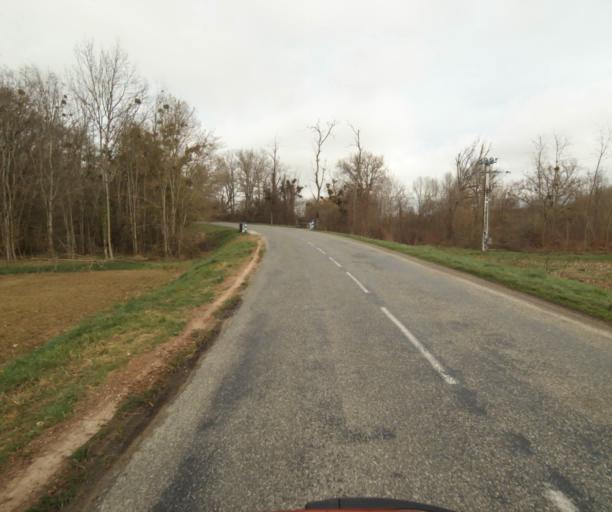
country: FR
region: Midi-Pyrenees
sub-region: Departement de l'Ariege
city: Pamiers
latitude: 43.1102
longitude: 1.5475
